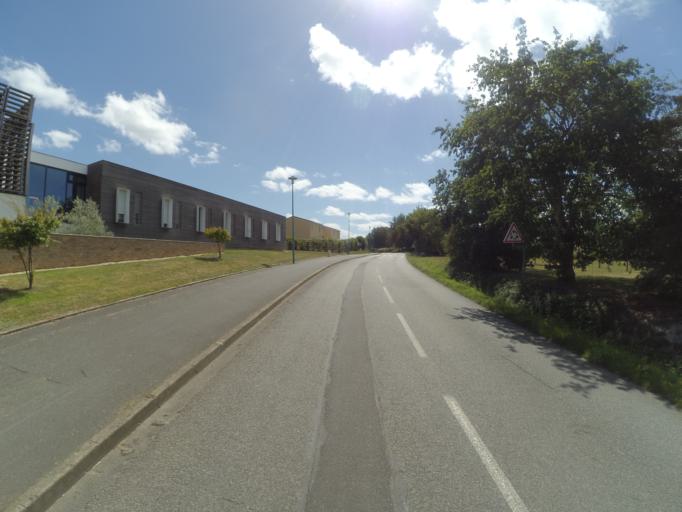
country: FR
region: Pays de la Loire
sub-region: Departement de la Loire-Atlantique
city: Aigrefeuille-sur-Maine
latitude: 47.0719
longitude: -1.4005
